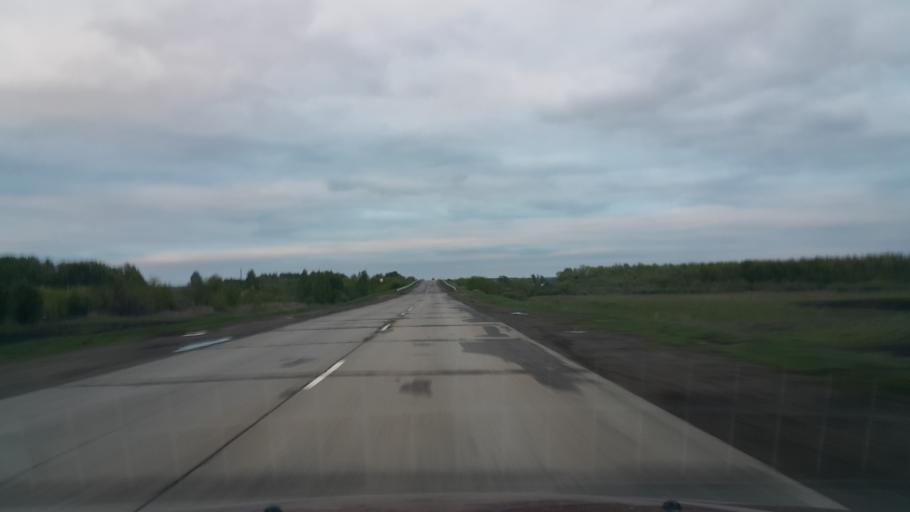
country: RU
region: Tambov
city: Kotovsk
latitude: 52.5750
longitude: 41.4442
